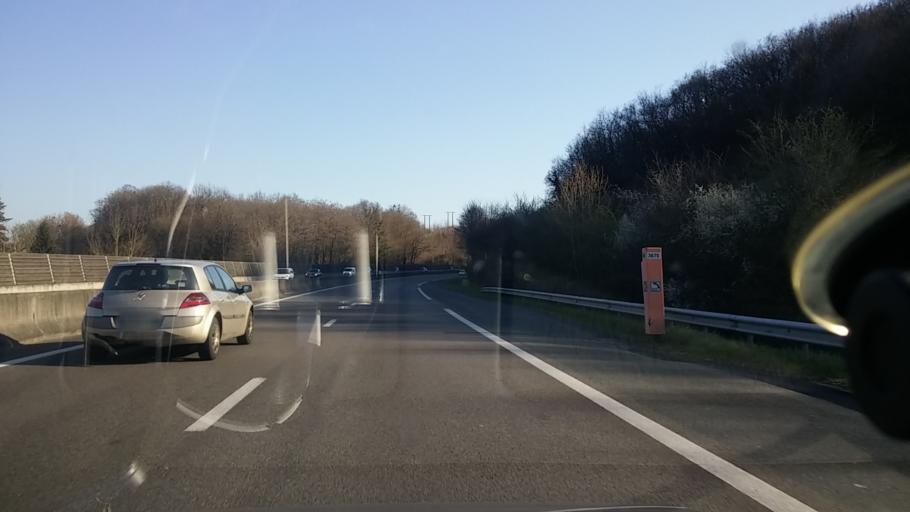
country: FR
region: Centre
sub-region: Departement de l'Indre
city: Saint-Marcel
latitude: 46.5992
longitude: 1.4989
